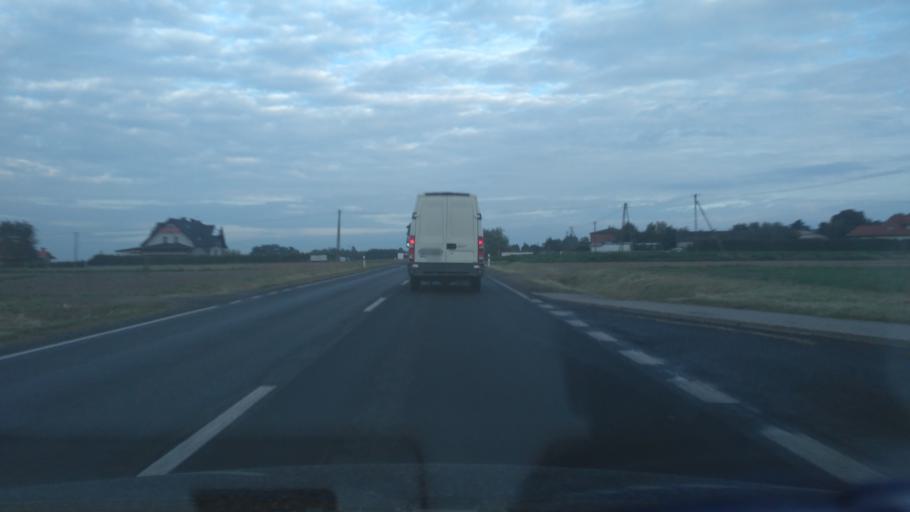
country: PL
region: Lublin Voivodeship
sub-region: Powiat leczynski
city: Spiczyn
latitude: 51.2997
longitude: 22.7612
